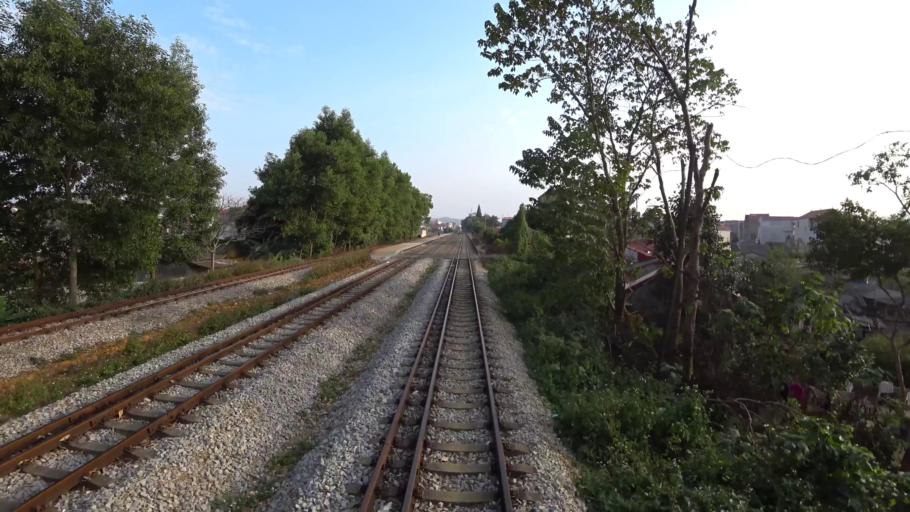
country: VN
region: Lang Son
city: Thi Tran Cao Loc
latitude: 21.8689
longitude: 106.7617
